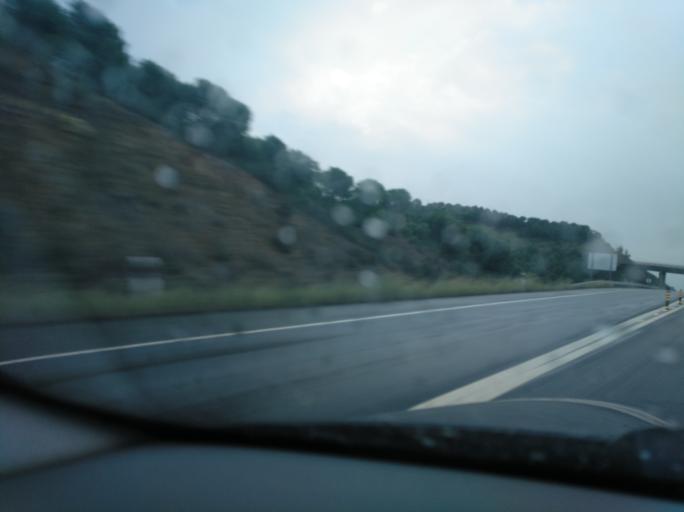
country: PT
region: Faro
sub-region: Castro Marim
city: Castro Marim
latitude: 37.3397
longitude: -7.5028
